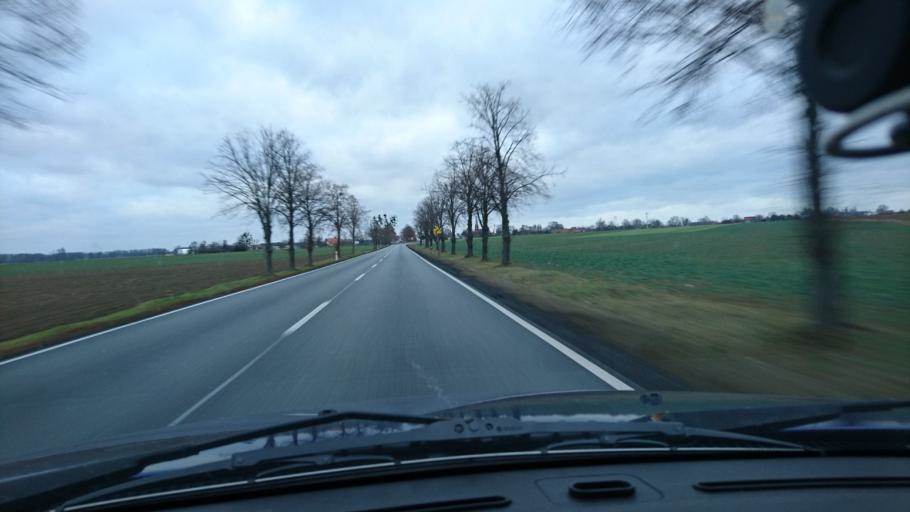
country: PL
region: Opole Voivodeship
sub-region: Powiat kluczborski
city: Kluczbork
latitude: 51.0207
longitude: 18.1959
